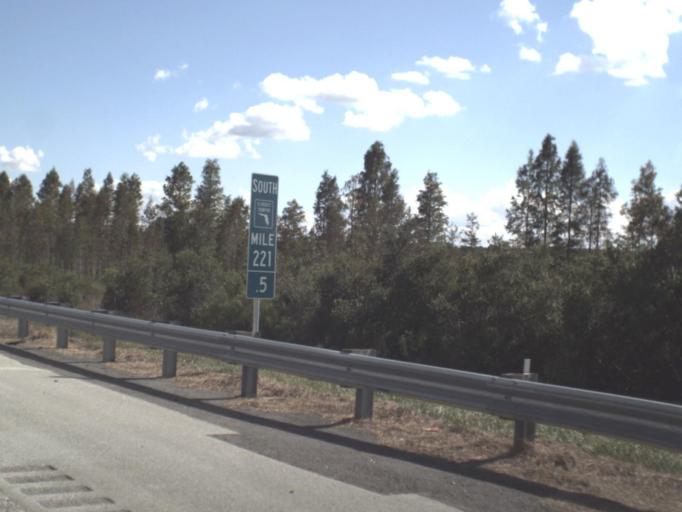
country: US
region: Florida
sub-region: Osceola County
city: Saint Cloud
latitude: 28.0115
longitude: -81.1681
